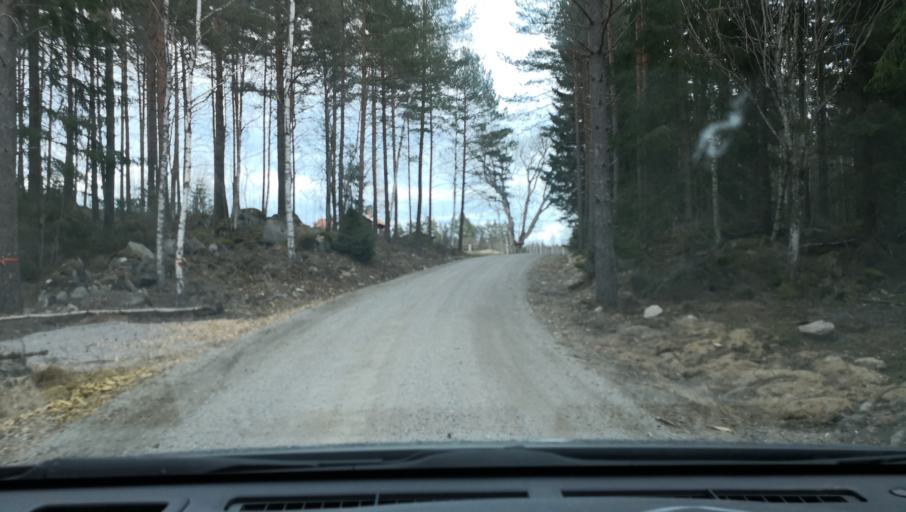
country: SE
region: Soedermanland
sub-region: Katrineholms Kommun
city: Katrineholm
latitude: 59.1309
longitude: 16.1562
